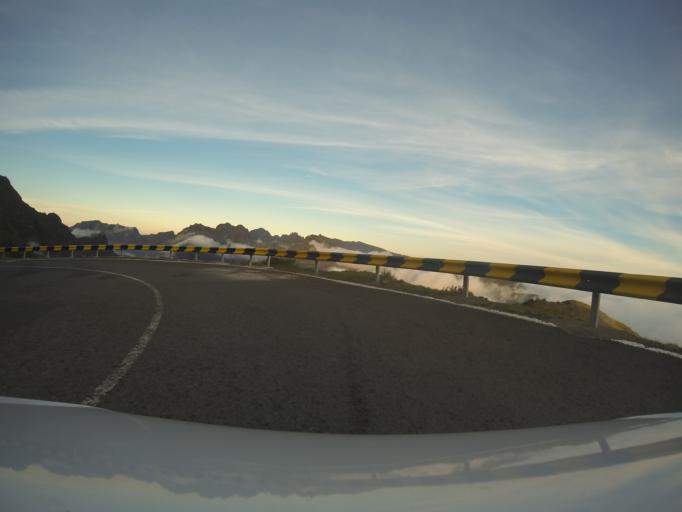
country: PT
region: Madeira
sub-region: Sao Vicente
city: Sao Vicente
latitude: 32.7341
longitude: -17.0530
